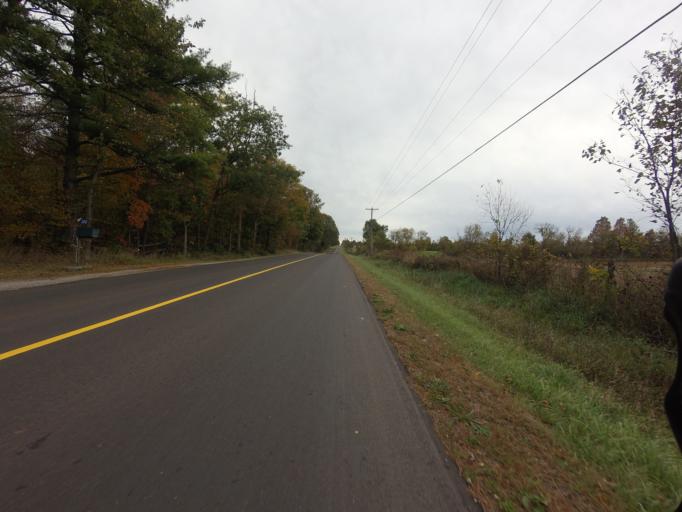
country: CA
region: Ontario
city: Gananoque
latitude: 44.5818
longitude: -76.0572
